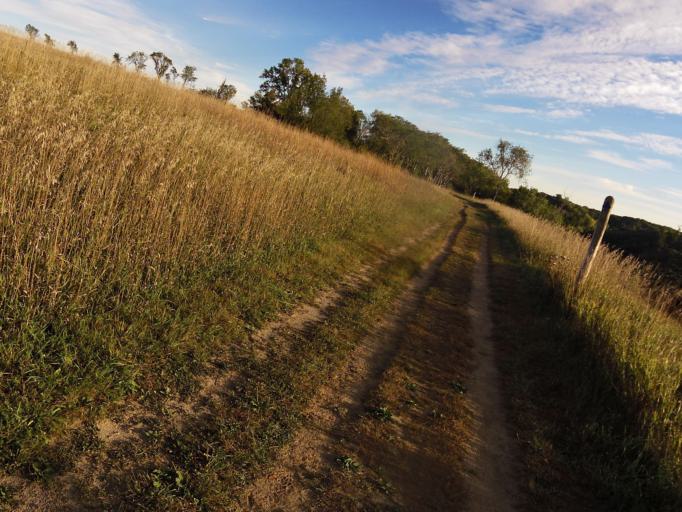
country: US
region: Minnesota
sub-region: Washington County
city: Afton
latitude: 44.8634
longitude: -92.7918
